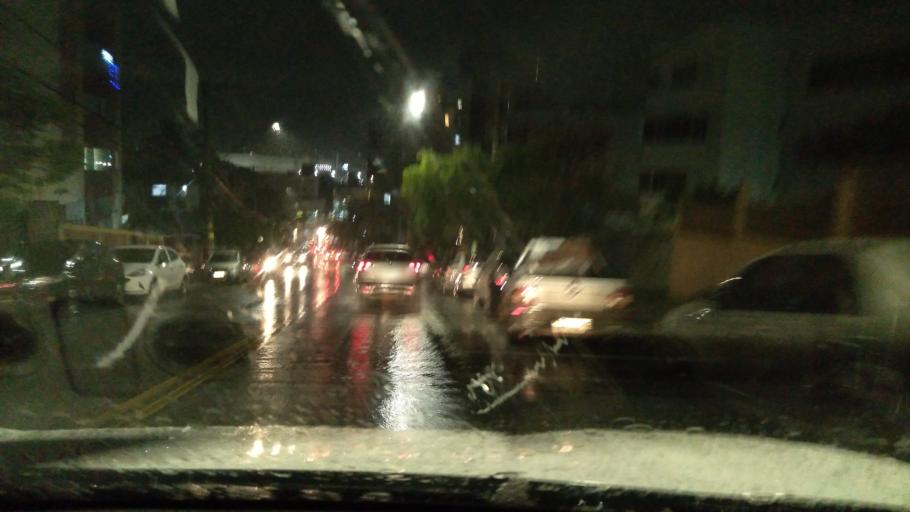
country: BR
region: Minas Gerais
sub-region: Belo Horizonte
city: Belo Horizonte
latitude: -19.8753
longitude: -43.9356
